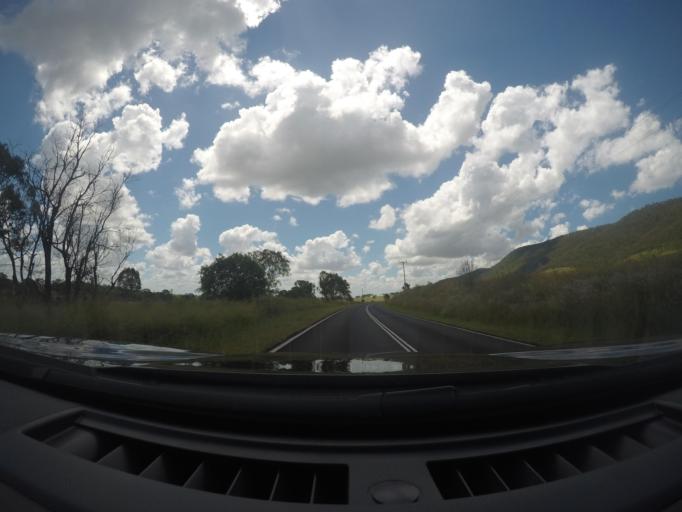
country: AU
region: Queensland
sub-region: Moreton Bay
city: Woodford
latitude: -27.1483
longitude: 152.5278
